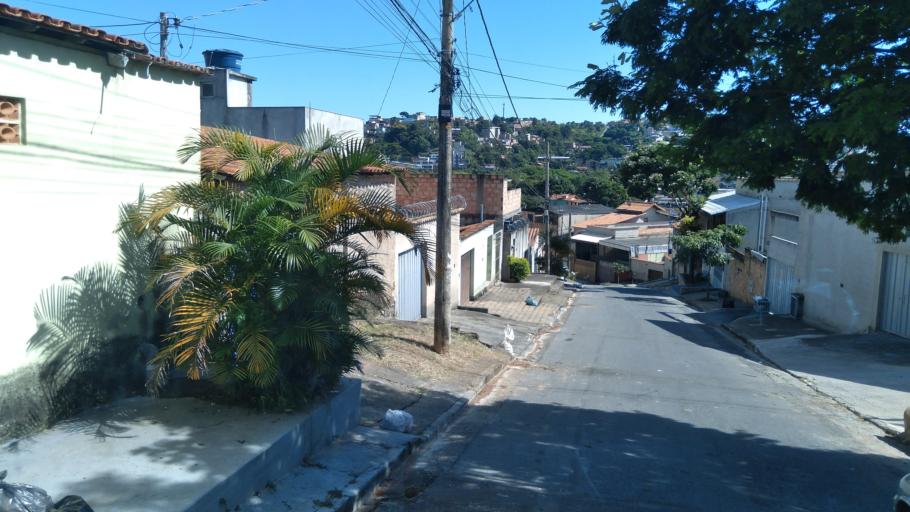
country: BR
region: Minas Gerais
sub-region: Belo Horizonte
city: Belo Horizonte
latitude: -19.8460
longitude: -43.9030
